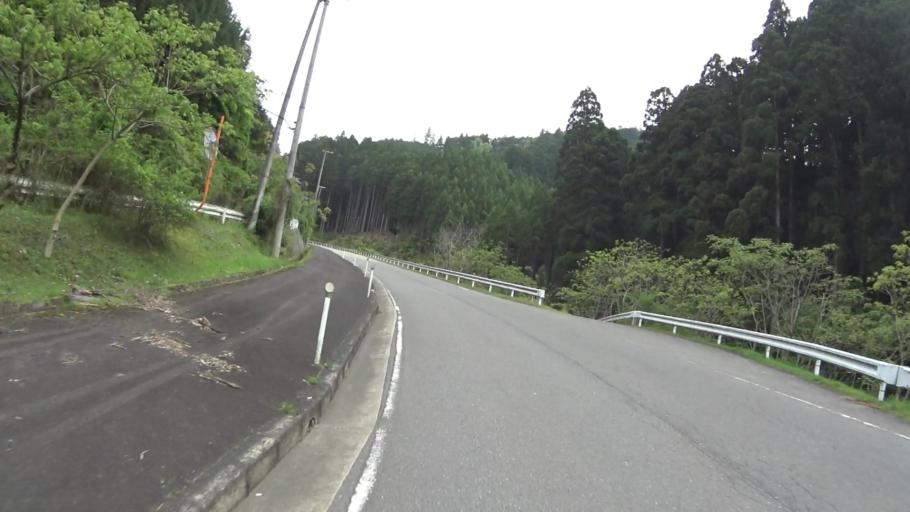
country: JP
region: Kyoto
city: Kameoka
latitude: 35.1313
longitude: 135.6196
